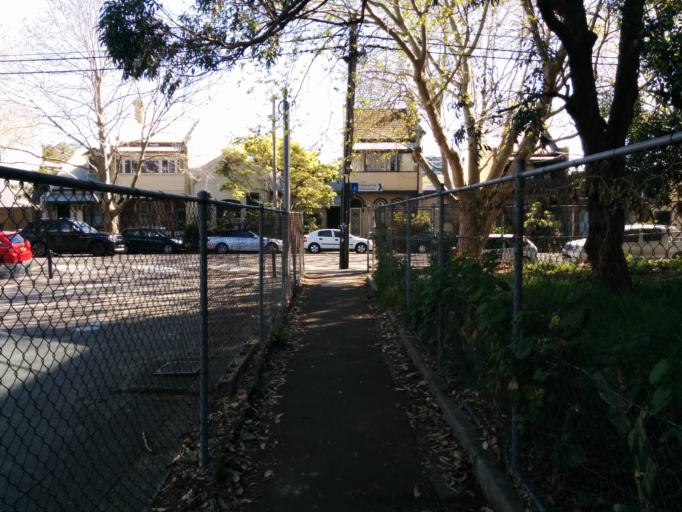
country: AU
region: New South Wales
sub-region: City of Sydney
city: Alexandria
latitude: -33.9003
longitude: 151.1947
